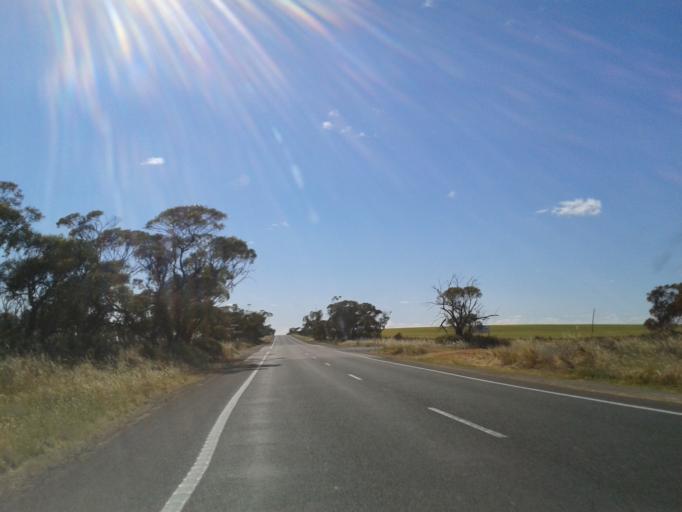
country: AU
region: South Australia
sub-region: Renmark Paringa
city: Renmark
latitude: -34.2757
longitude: 141.3334
